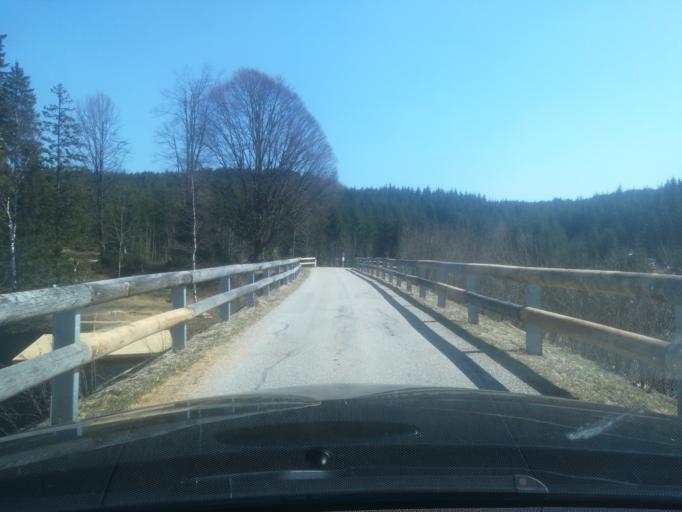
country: AT
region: Lower Austria
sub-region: Politischer Bezirk Zwettl
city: Langschlag
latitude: 48.4990
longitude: 14.8544
